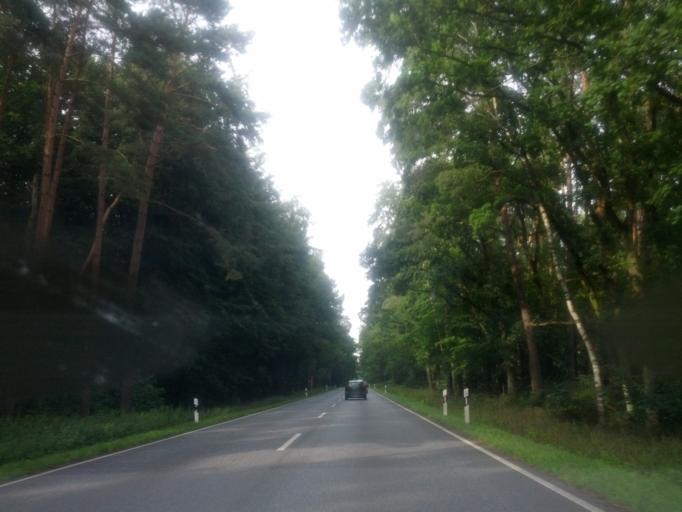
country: DE
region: Mecklenburg-Vorpommern
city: Neubukow
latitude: 53.9987
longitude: 11.6394
